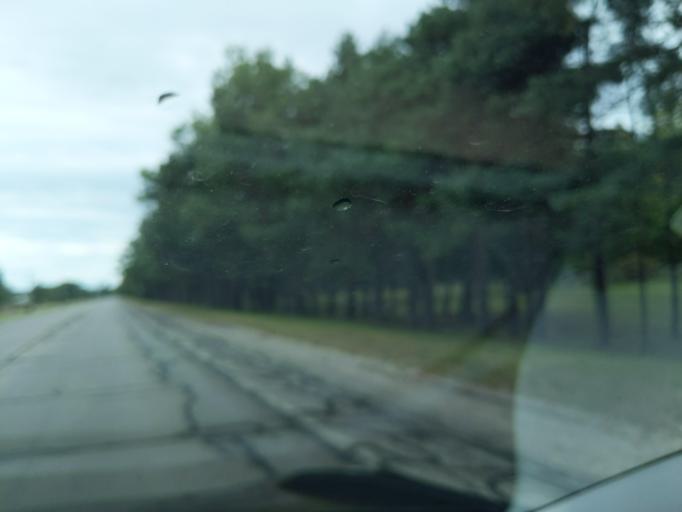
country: US
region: Michigan
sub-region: Grand Traverse County
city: Traverse City
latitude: 44.7526
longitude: -85.5847
